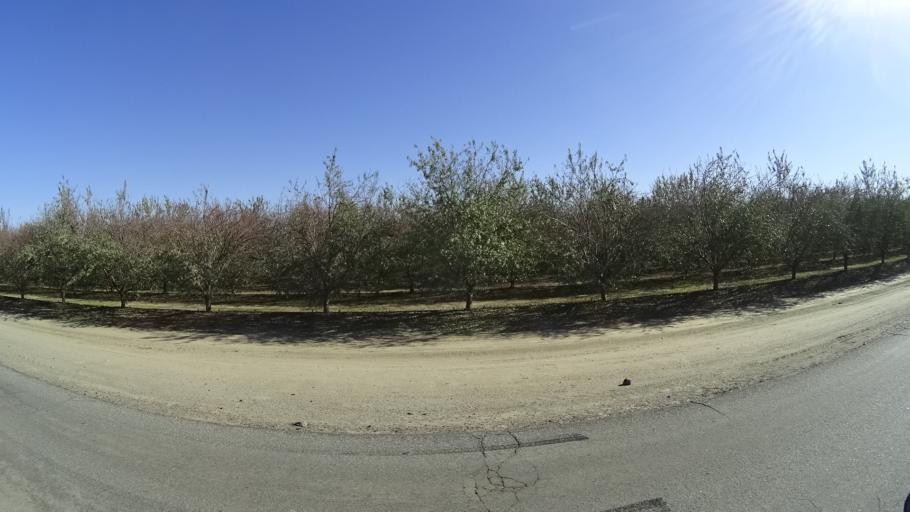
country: US
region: California
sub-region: Kern County
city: Greenfield
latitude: 35.2466
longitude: -119.0568
